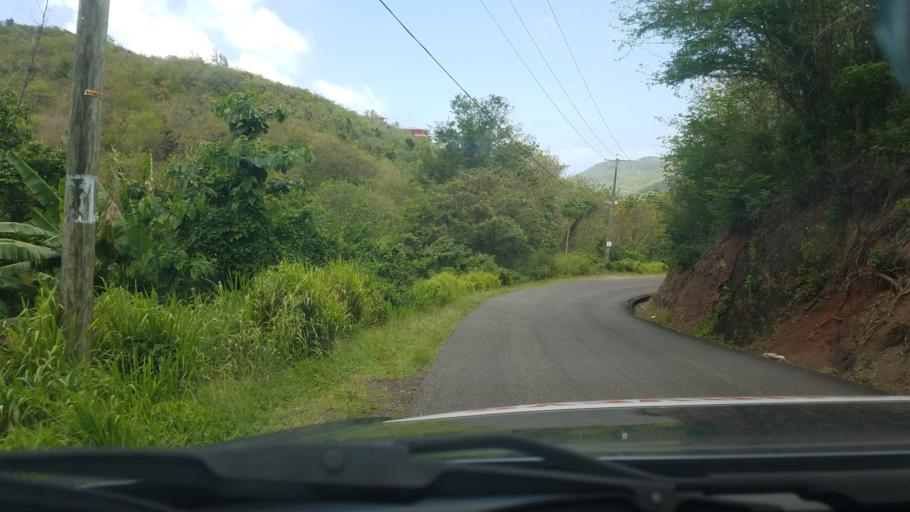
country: LC
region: Gros-Islet
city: Gros Islet
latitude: 14.0559
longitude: -60.9344
